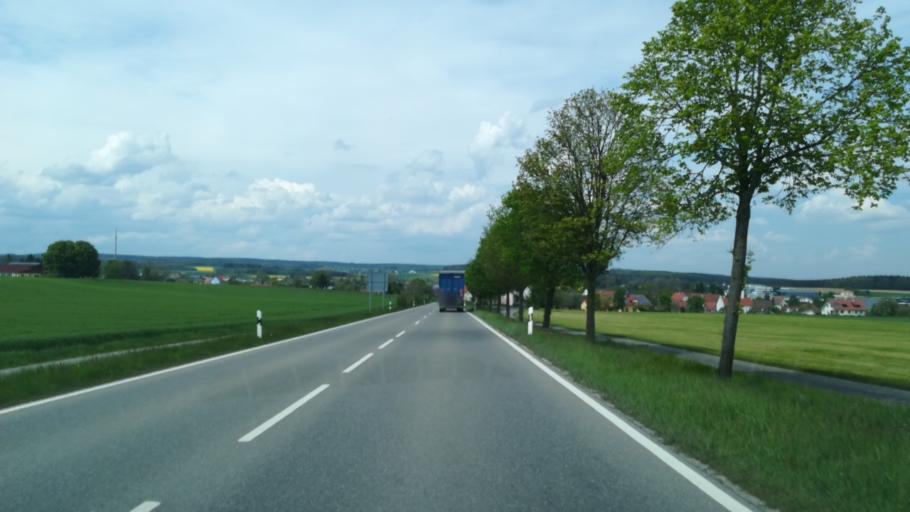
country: DE
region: Baden-Wuerttemberg
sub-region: Freiburg Region
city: Muhlingen
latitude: 47.9557
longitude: 9.0446
